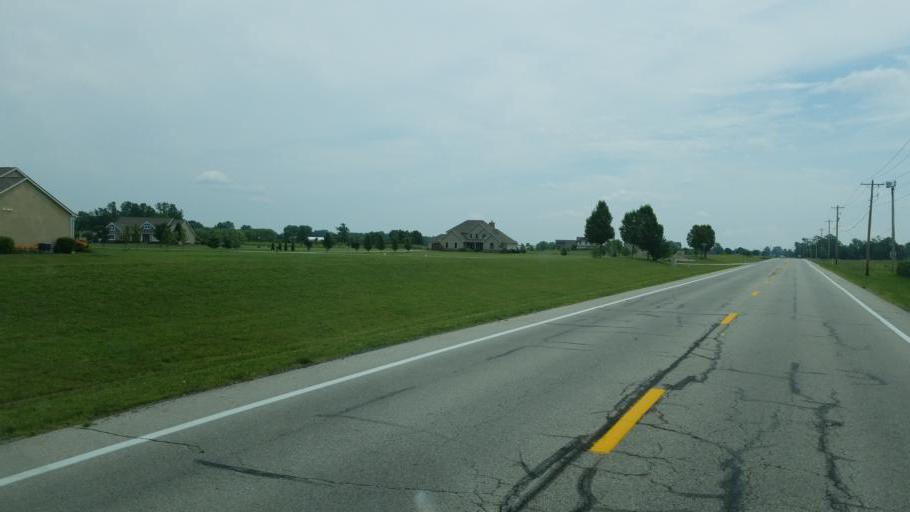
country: US
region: Ohio
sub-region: Franklin County
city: Hilliard
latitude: 40.0368
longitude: -83.2231
